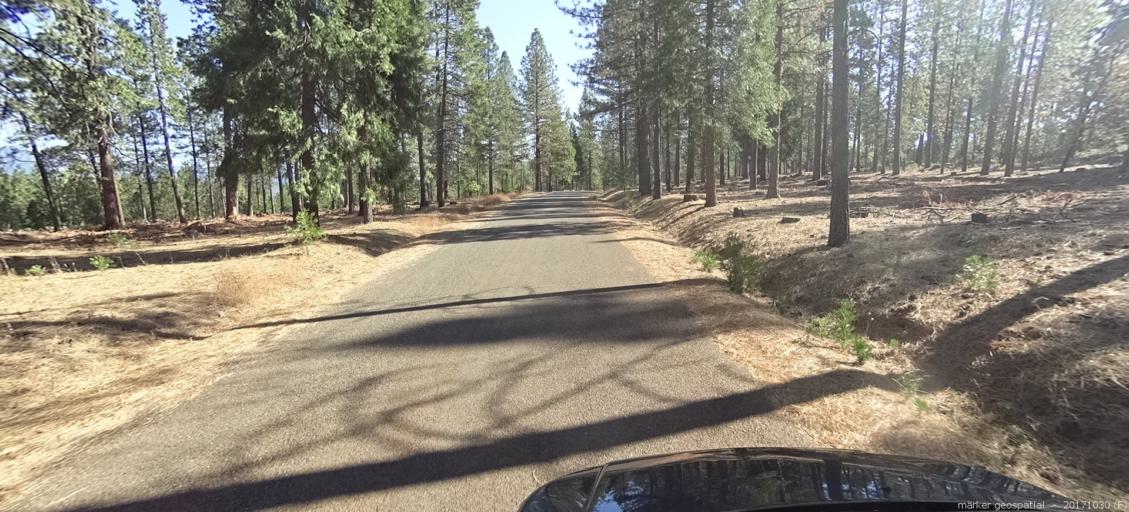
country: US
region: California
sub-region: Shasta County
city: Shingletown
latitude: 40.6189
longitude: -121.8915
